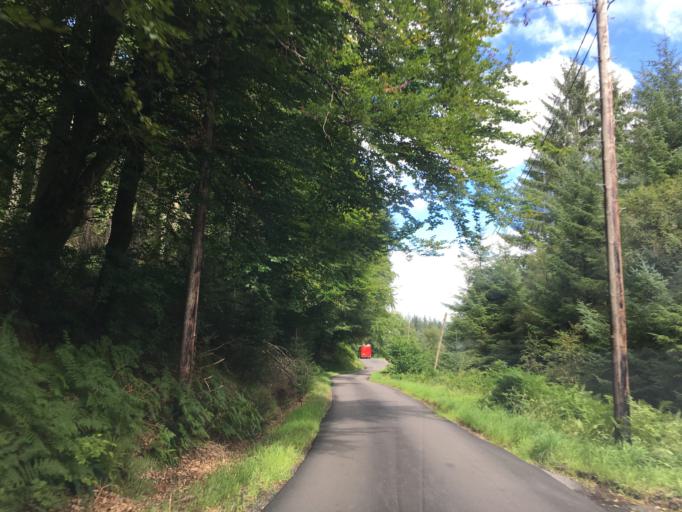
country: GB
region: Scotland
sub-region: Argyll and Bute
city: Oban
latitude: 56.2868
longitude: -5.2678
